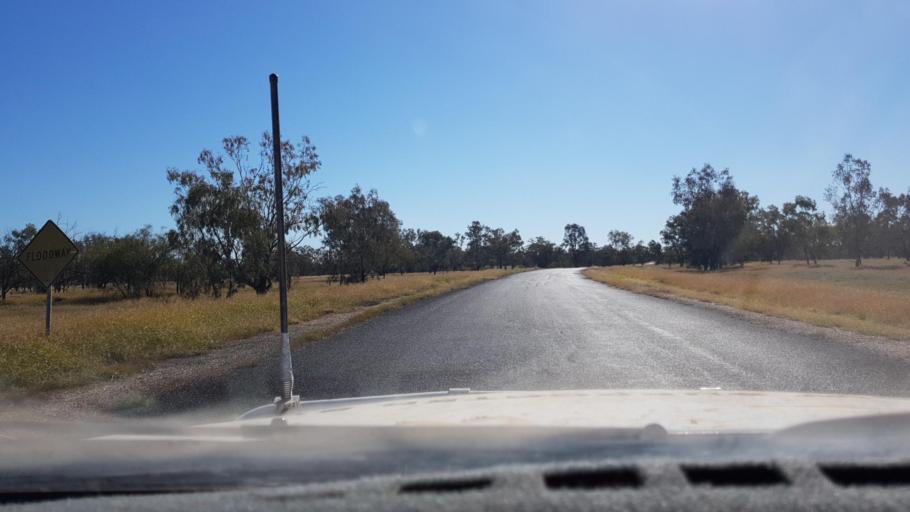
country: AU
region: New South Wales
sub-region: Walgett
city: Lightning Ridge
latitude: -29.5682
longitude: 148.6630
